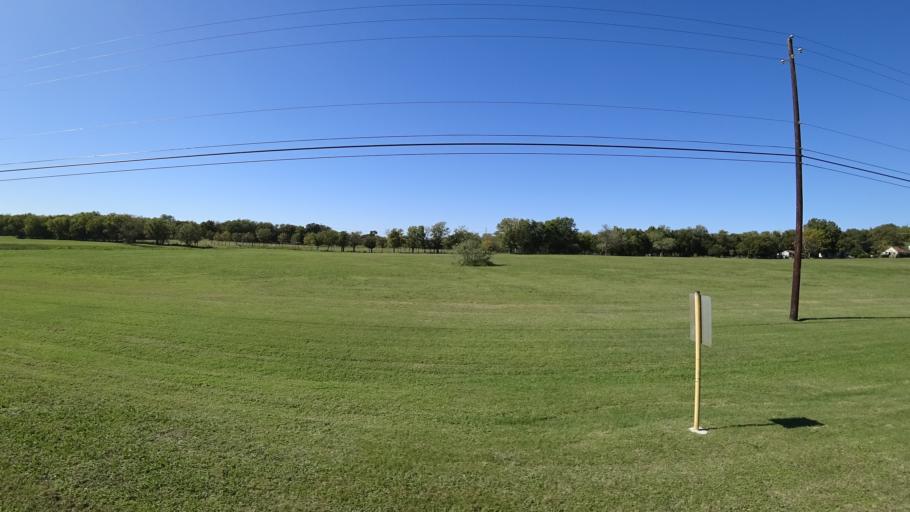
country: US
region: Texas
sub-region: Travis County
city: Hornsby Bend
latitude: 30.2766
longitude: -97.6432
